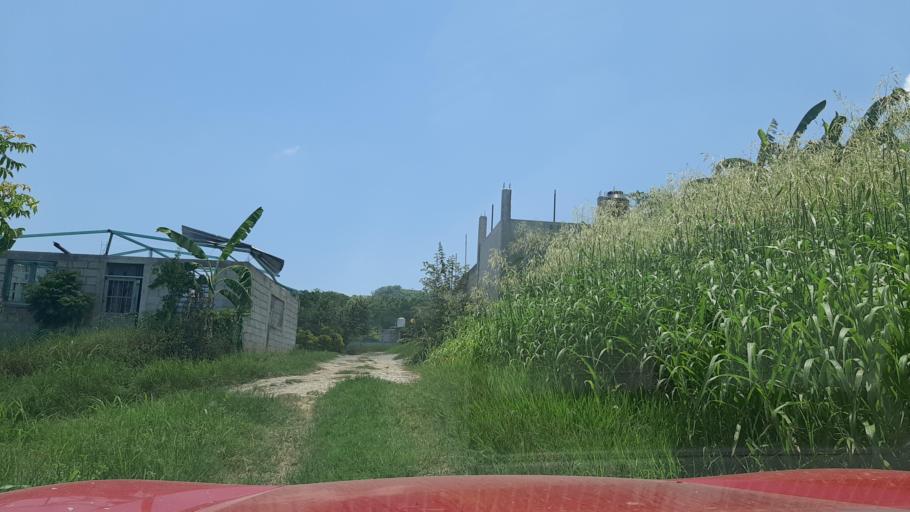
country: MX
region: Veracruz
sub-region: Poza Rica de Hidalgo
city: El Mollejon
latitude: 20.5441
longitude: -97.4106
